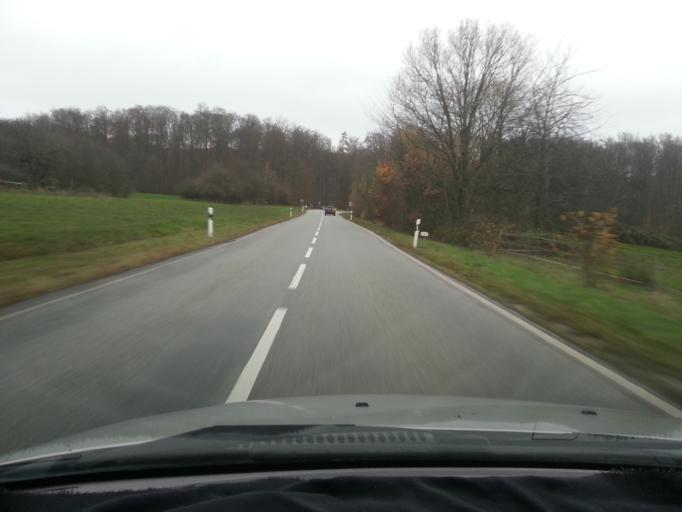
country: DE
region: Baden-Wuerttemberg
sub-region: Karlsruhe Region
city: Gaiberg
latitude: 49.3654
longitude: 8.7421
